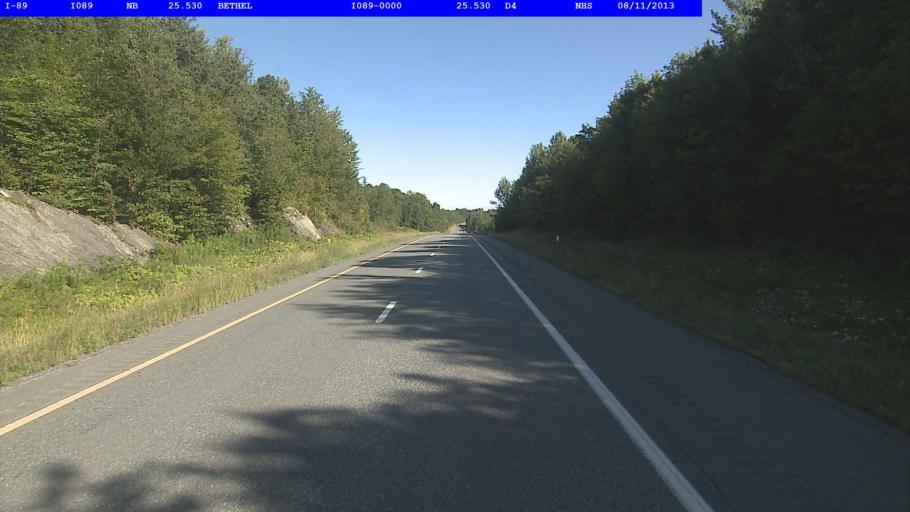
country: US
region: Vermont
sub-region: Orange County
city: Randolph
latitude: 43.8688
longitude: -72.6098
